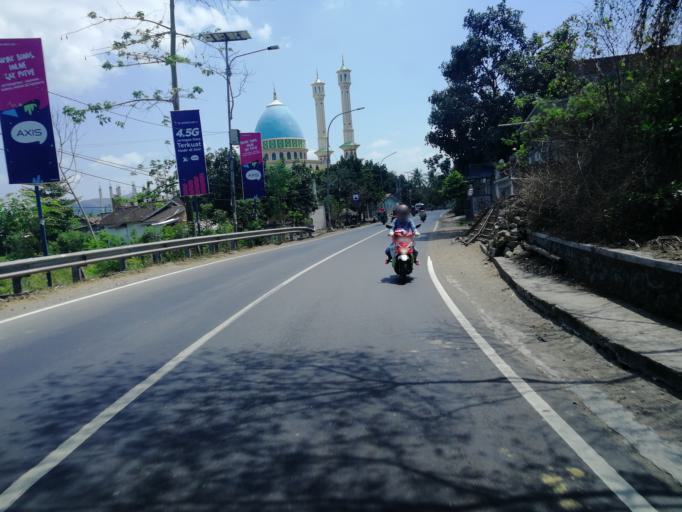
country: ID
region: West Nusa Tenggara
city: Jelateng Timur
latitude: -8.7085
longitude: 116.0783
